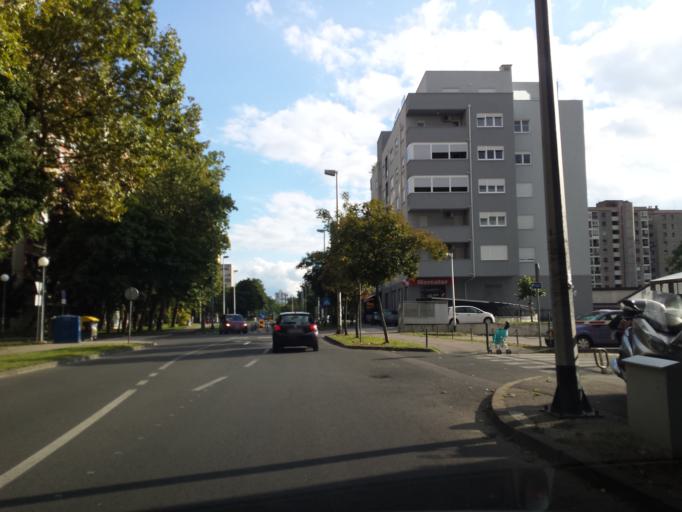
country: HR
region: Grad Zagreb
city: Novi Zagreb
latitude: 45.7919
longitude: 15.9947
